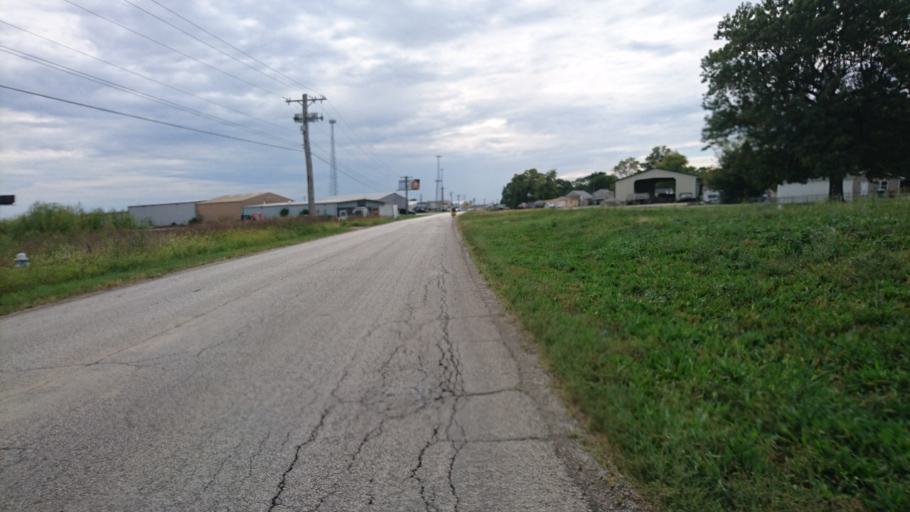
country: US
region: Illinois
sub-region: Sangamon County
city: Southern View
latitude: 39.7686
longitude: -89.6576
